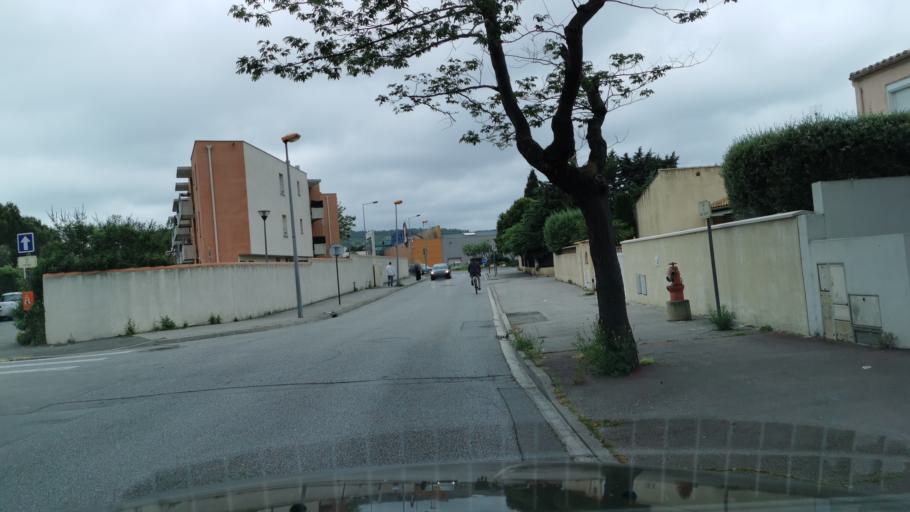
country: FR
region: Languedoc-Roussillon
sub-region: Departement de l'Aude
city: Narbonne
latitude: 43.1856
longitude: 2.9839
